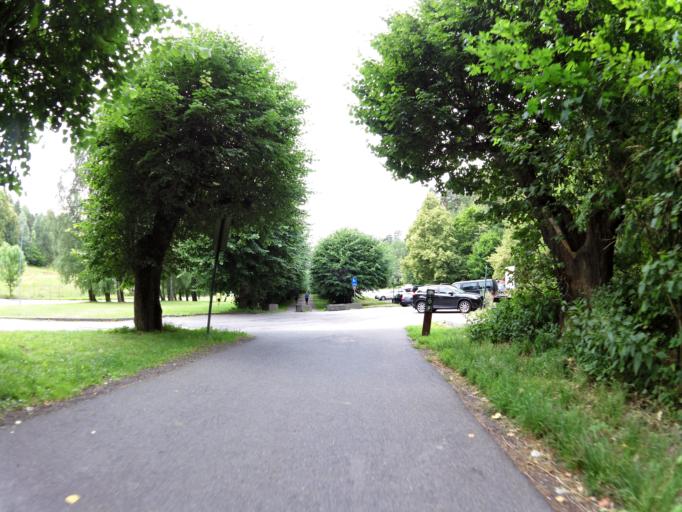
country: NO
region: Akershus
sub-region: Oppegard
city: Kolbotn
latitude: 59.8366
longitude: 10.7765
